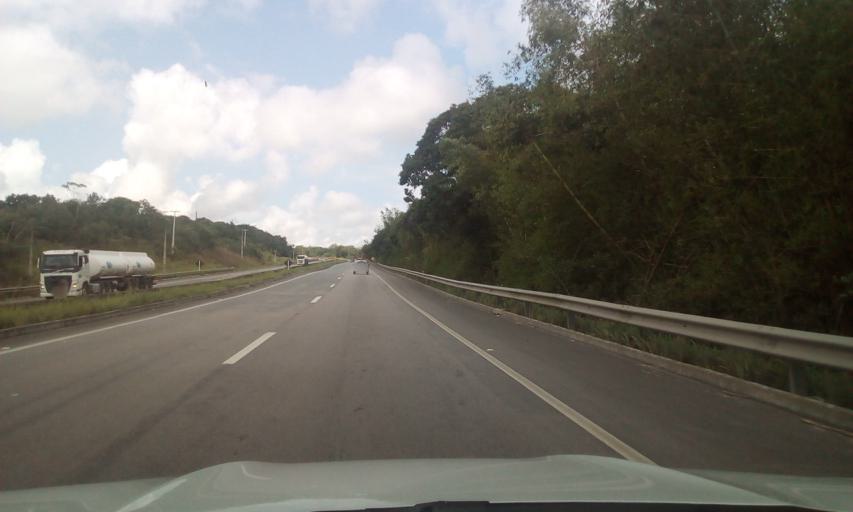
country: BR
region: Paraiba
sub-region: Alhandra
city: Alhandra
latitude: -7.4349
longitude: -34.9719
